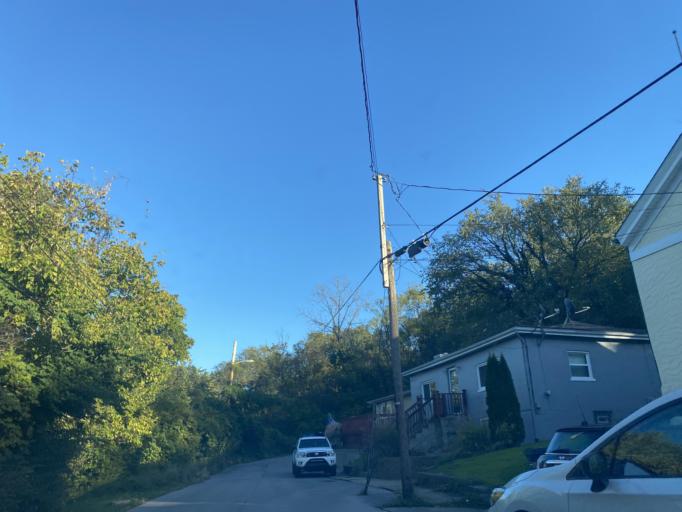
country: US
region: Kentucky
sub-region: Campbell County
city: Dayton
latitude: 39.1130
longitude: -84.4603
